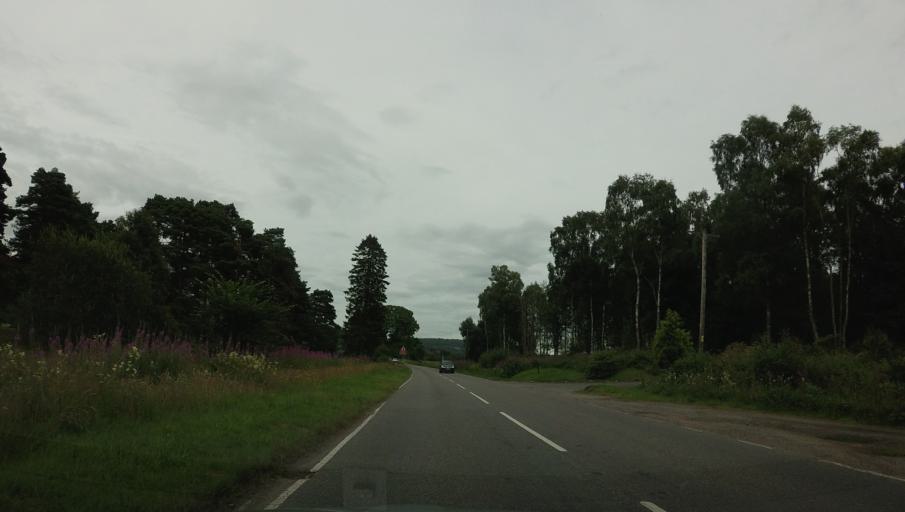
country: GB
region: Scotland
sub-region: Aberdeenshire
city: Aboyne
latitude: 57.0858
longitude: -2.7213
